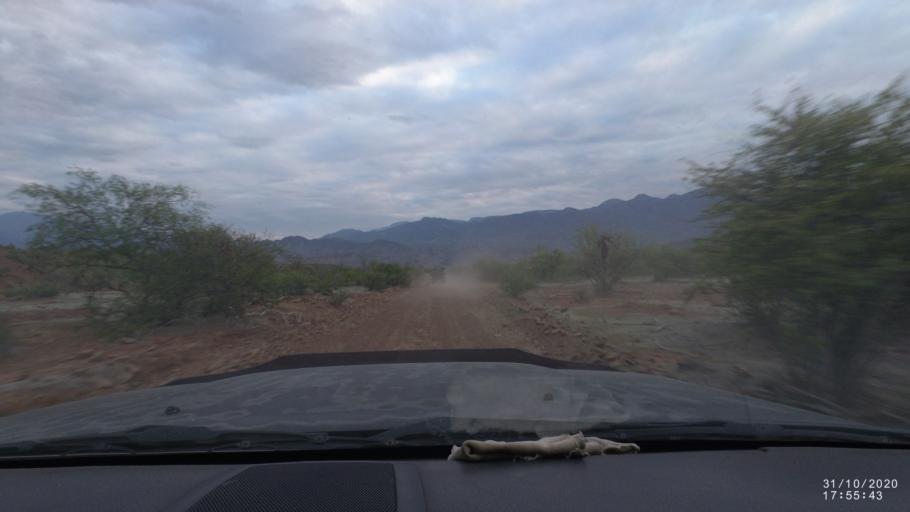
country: BO
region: Chuquisaca
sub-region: Provincia Zudanez
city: Mojocoya
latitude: -18.6461
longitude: -64.5284
